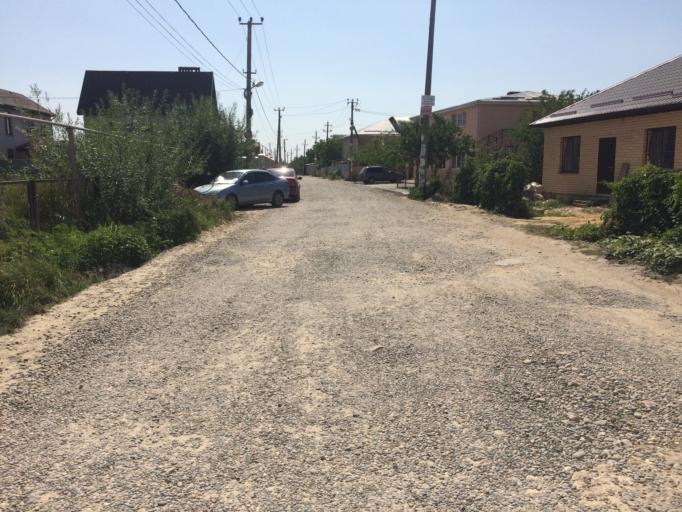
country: RU
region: Stavropol'skiy
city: Tatarka
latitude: 44.9878
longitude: 41.9400
